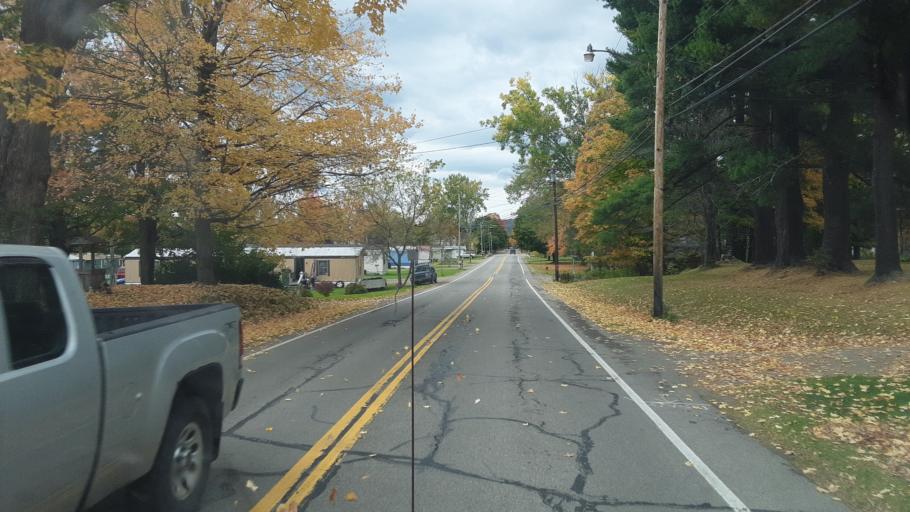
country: US
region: New York
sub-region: Allegany County
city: Belmont
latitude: 42.3033
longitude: -78.0058
